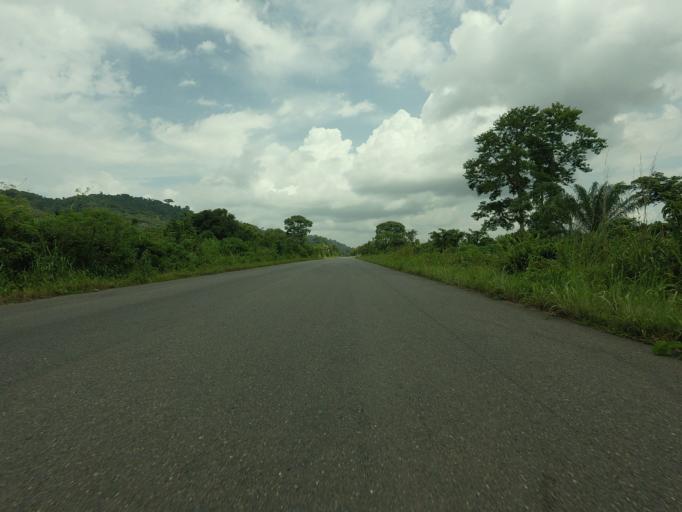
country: GH
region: Volta
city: Ho
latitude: 6.4895
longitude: 0.2000
